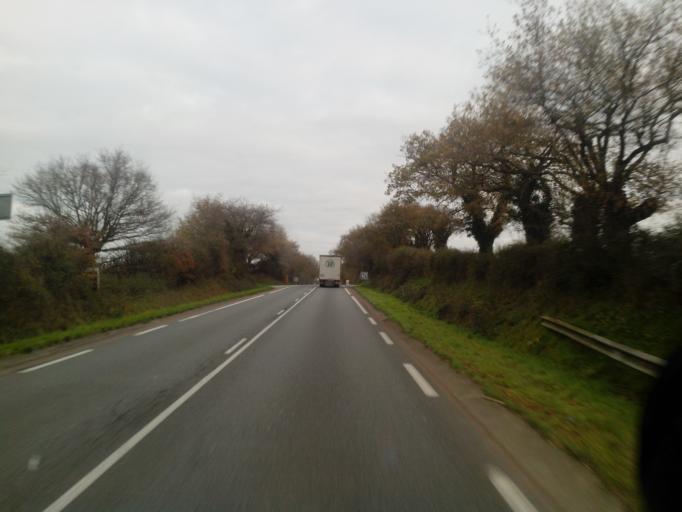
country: FR
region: Poitou-Charentes
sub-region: Departement des Deux-Sevres
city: Chatillon-sur-Thouet
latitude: 46.6479
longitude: -0.2027
